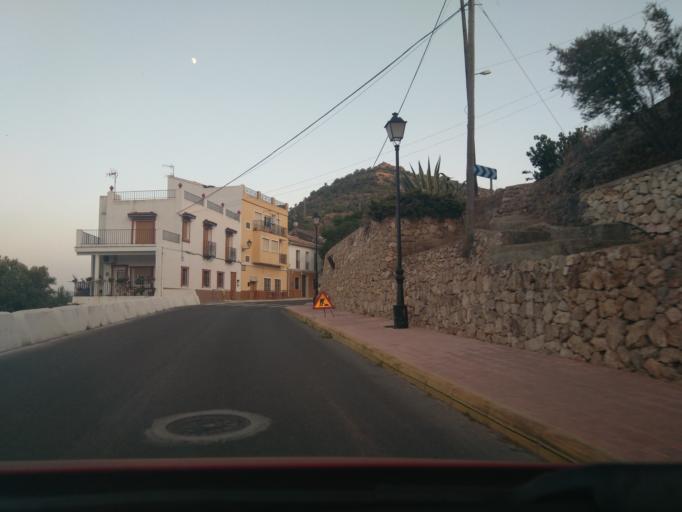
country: ES
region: Valencia
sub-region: Provincia de Valencia
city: Sumacarcer
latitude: 39.0925
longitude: -0.6285
